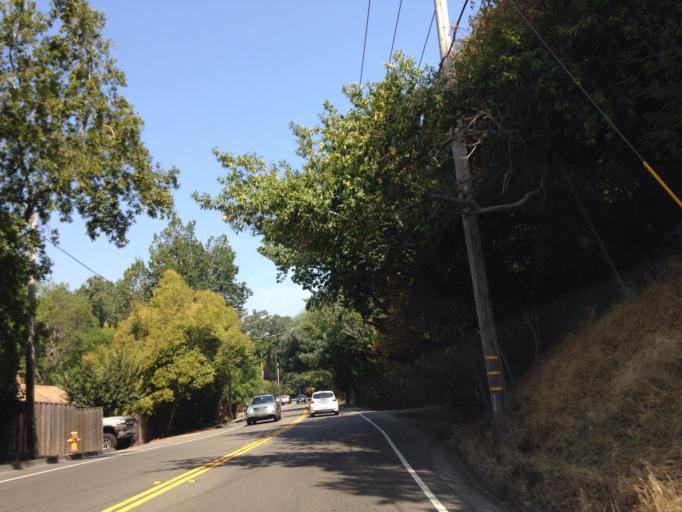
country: US
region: California
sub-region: Marin County
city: Ross
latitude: 37.9658
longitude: -122.5583
